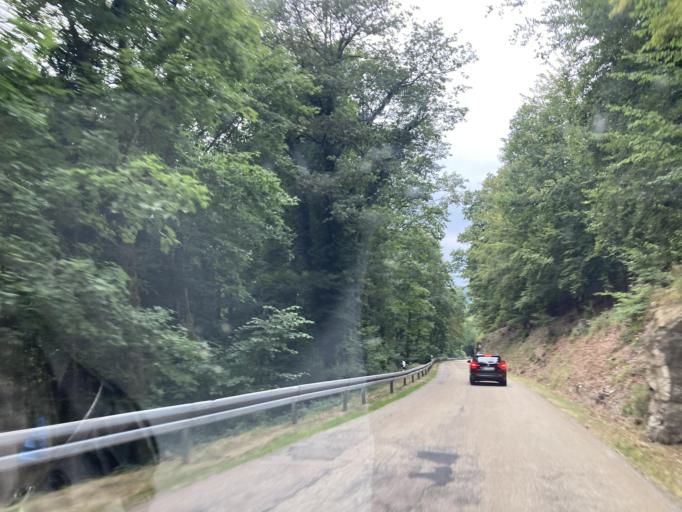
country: DE
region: Baden-Wuerttemberg
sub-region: Freiburg Region
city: Sulzburg
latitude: 47.8038
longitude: 7.7147
